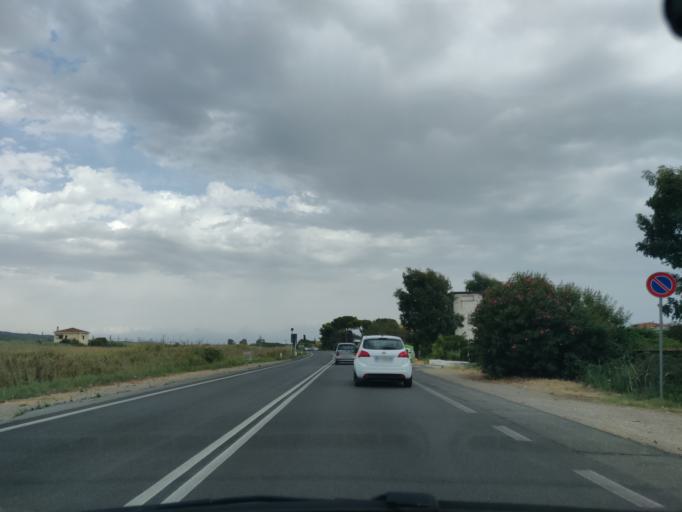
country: IT
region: Latium
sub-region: Citta metropolitana di Roma Capitale
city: Santa Marinella
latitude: 42.0373
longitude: 11.9213
